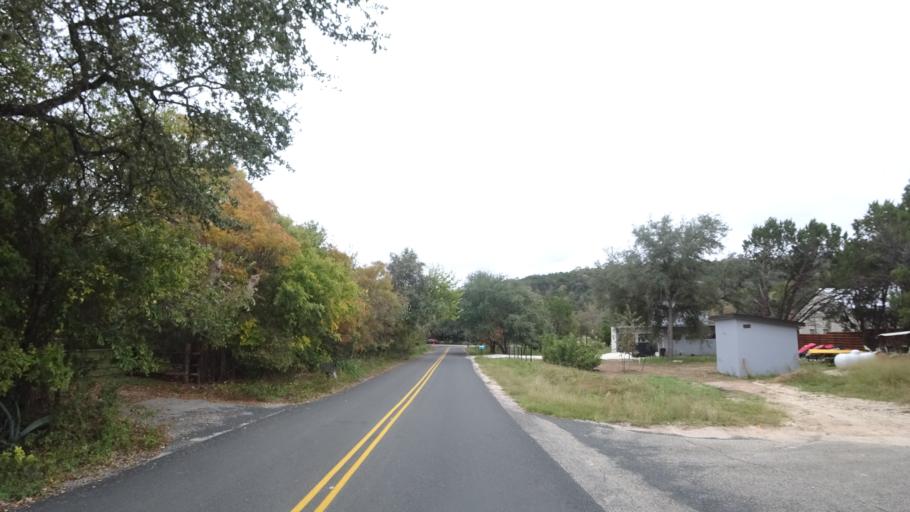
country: US
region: Texas
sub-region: Travis County
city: Bee Cave
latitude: 30.3543
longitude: -97.9199
